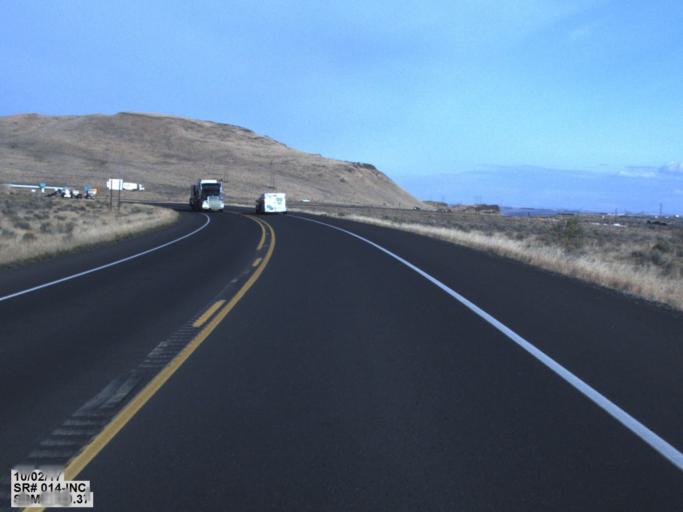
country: US
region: Oregon
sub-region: Umatilla County
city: Umatilla
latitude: 45.9439
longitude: -119.3429
